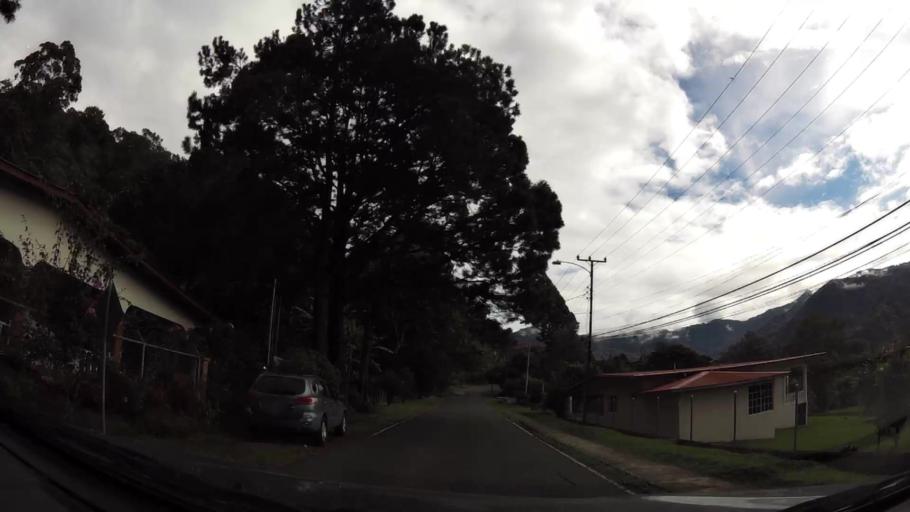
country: PA
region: Chiriqui
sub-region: Distrito Boquete
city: Boquete
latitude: 8.7972
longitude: -82.4388
